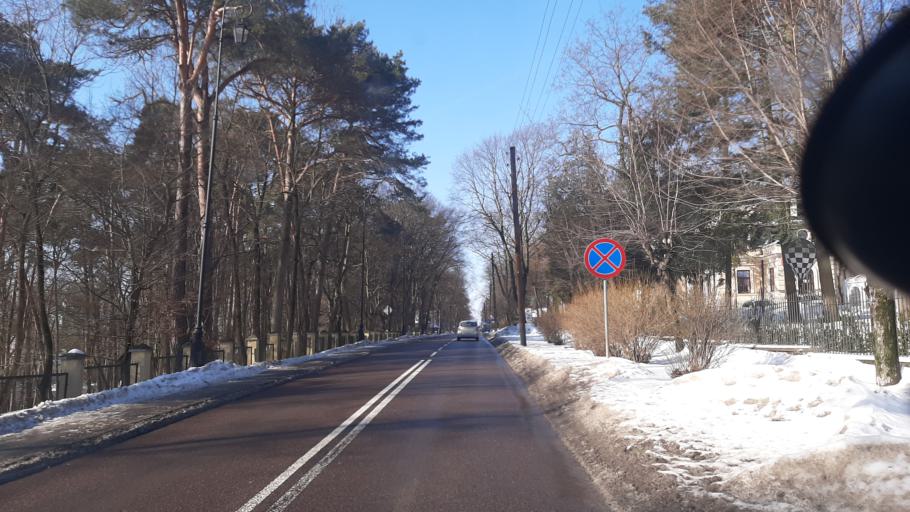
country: PL
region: Lublin Voivodeship
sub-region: Powiat pulawski
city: Naleczow
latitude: 51.2881
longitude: 22.2126
